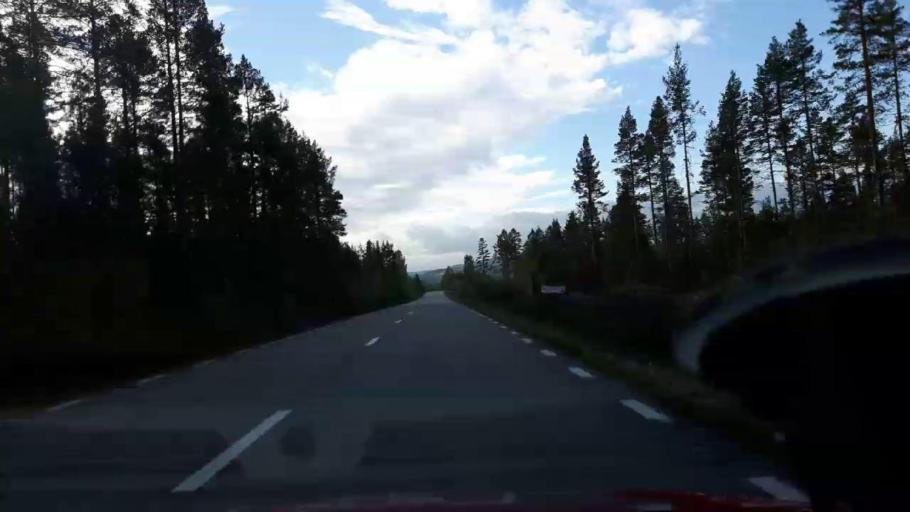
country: SE
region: Gaevleborg
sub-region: Ljusdals Kommun
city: Farila
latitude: 62.0095
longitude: 15.2405
